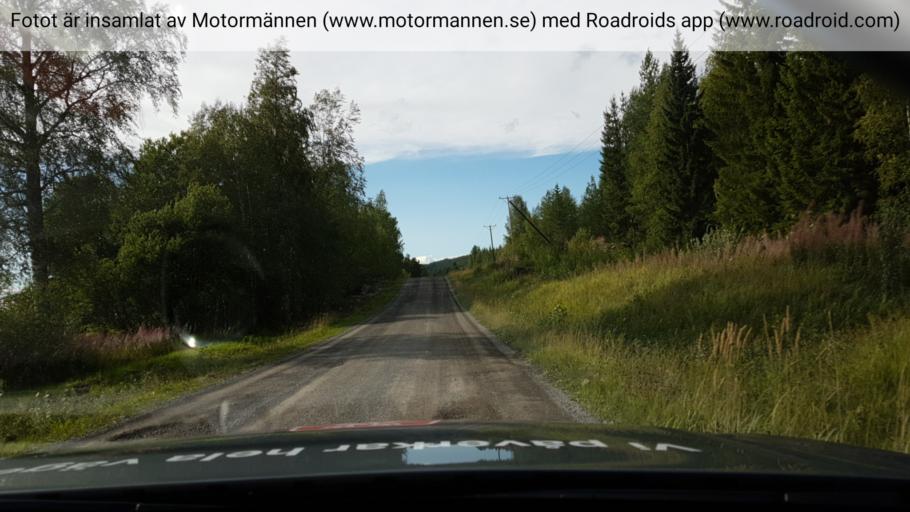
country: SE
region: Jaemtland
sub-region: Braecke Kommun
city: Braecke
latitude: 63.1927
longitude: 15.5137
